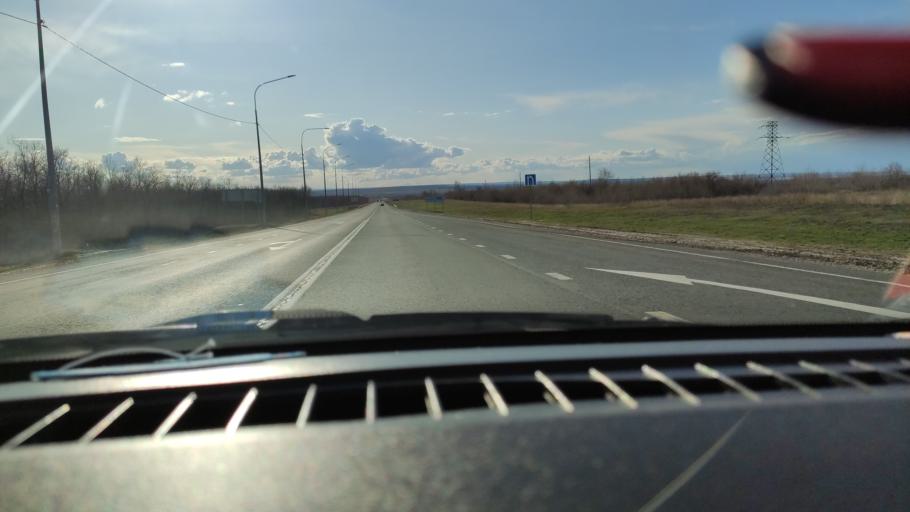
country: RU
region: Saratov
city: Yelshanka
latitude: 51.8264
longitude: 46.2812
